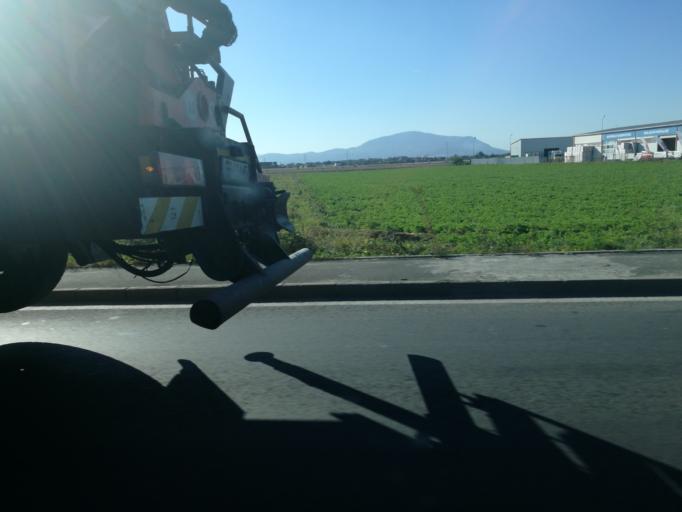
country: RO
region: Brasov
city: Brasov
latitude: 45.6877
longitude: 25.5828
